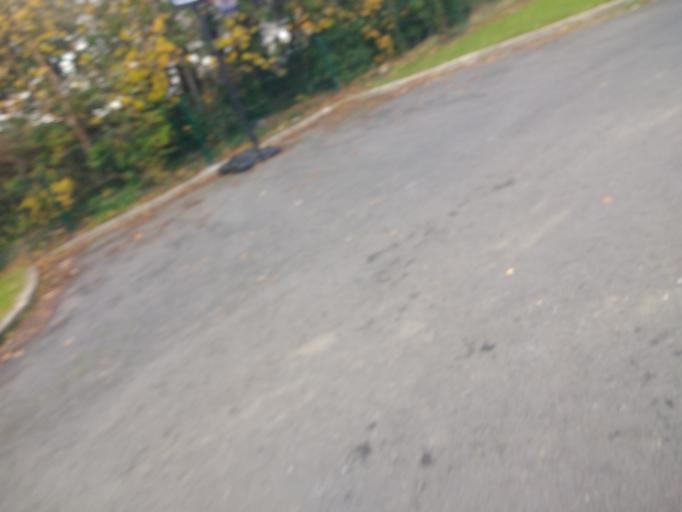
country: IE
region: Leinster
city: Kinsealy-Drinan
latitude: 53.4463
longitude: -6.1867
